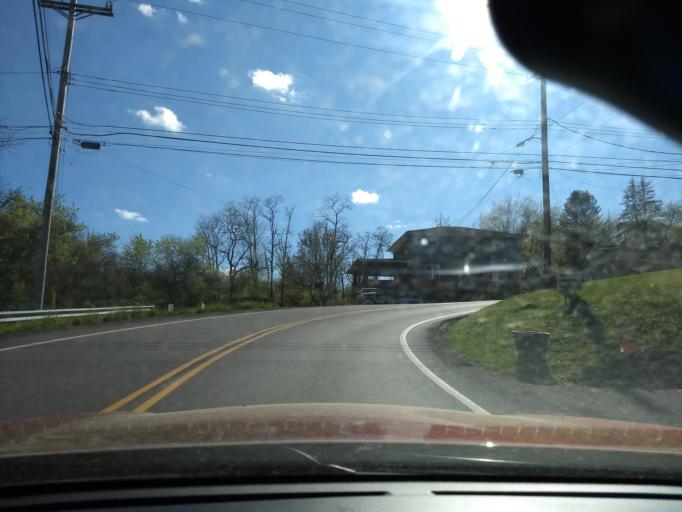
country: US
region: Pennsylvania
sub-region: Allegheny County
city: Brentwood
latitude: 40.3902
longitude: -79.9656
